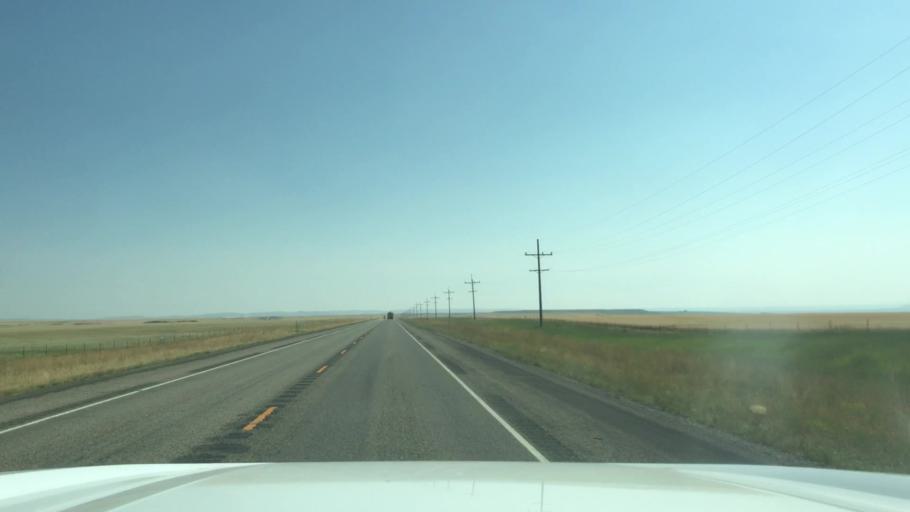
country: US
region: Montana
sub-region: Wheatland County
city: Harlowton
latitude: 46.5087
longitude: -109.7661
